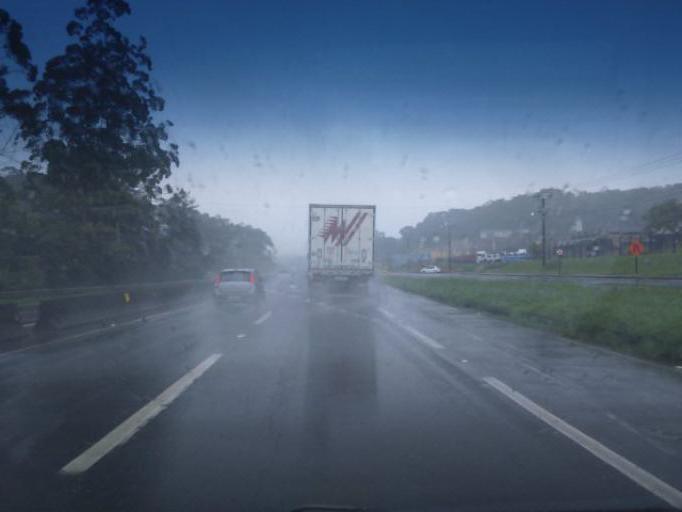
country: BR
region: Santa Catarina
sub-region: Joinville
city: Joinville
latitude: -26.3630
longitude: -48.8588
